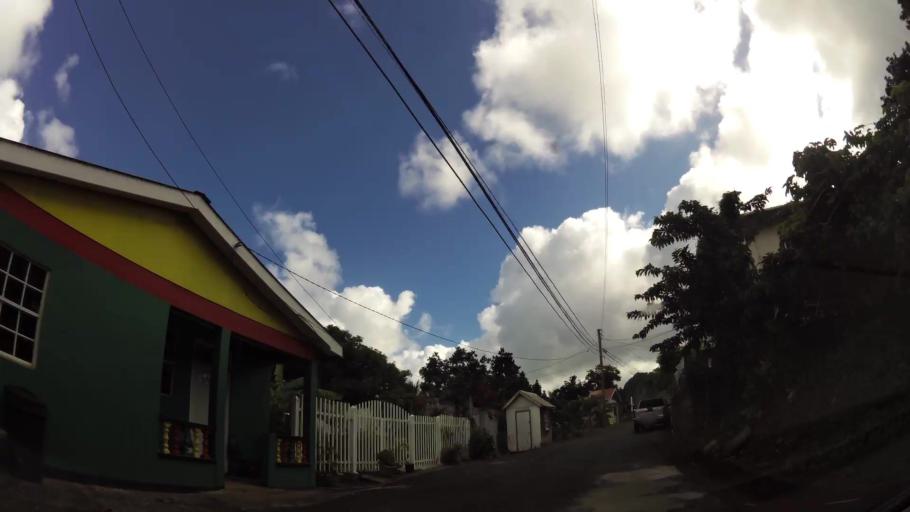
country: DM
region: Saint Andrew
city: Calibishie
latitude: 15.6144
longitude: -61.4039
